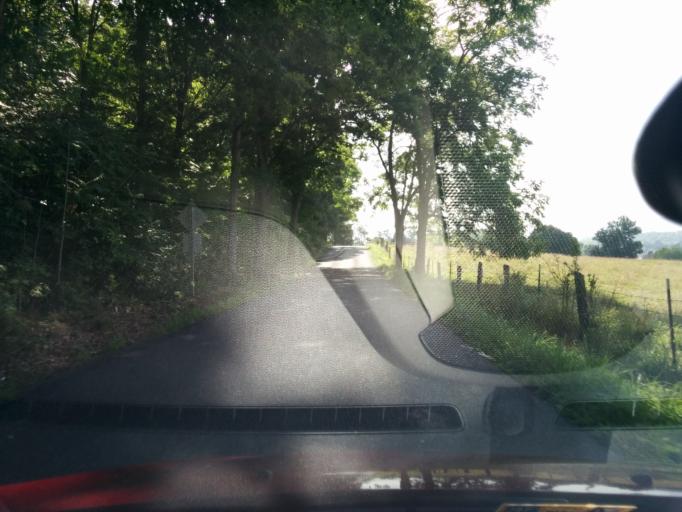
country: US
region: Virginia
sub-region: City of Lexington
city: Lexington
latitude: 37.7739
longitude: -79.4800
